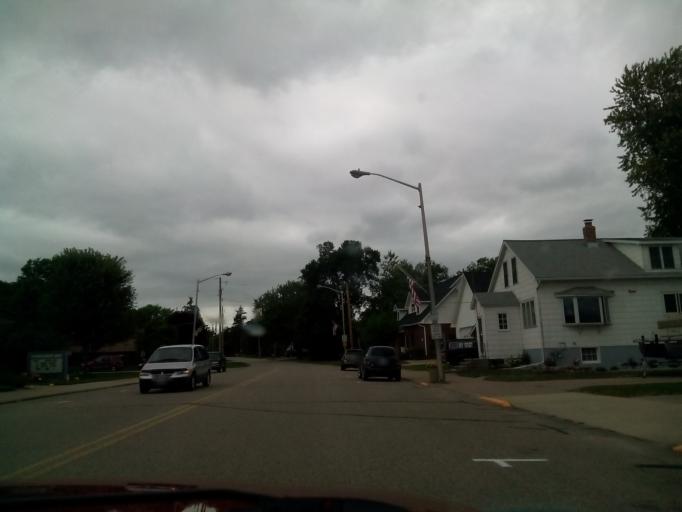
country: US
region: Wisconsin
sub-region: Waupaca County
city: Weyauwega
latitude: 44.2614
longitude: -88.8669
